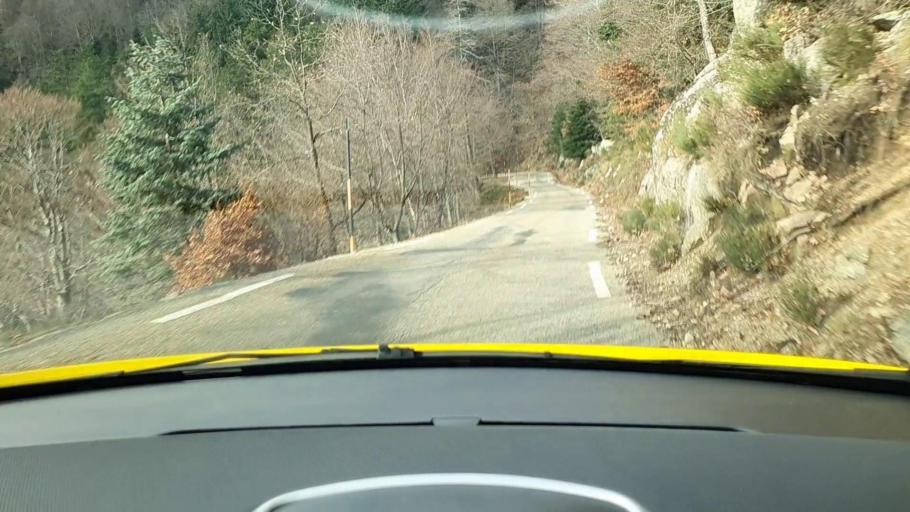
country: FR
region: Languedoc-Roussillon
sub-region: Departement du Gard
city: Branoux-les-Taillades
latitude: 44.3696
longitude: 3.9225
